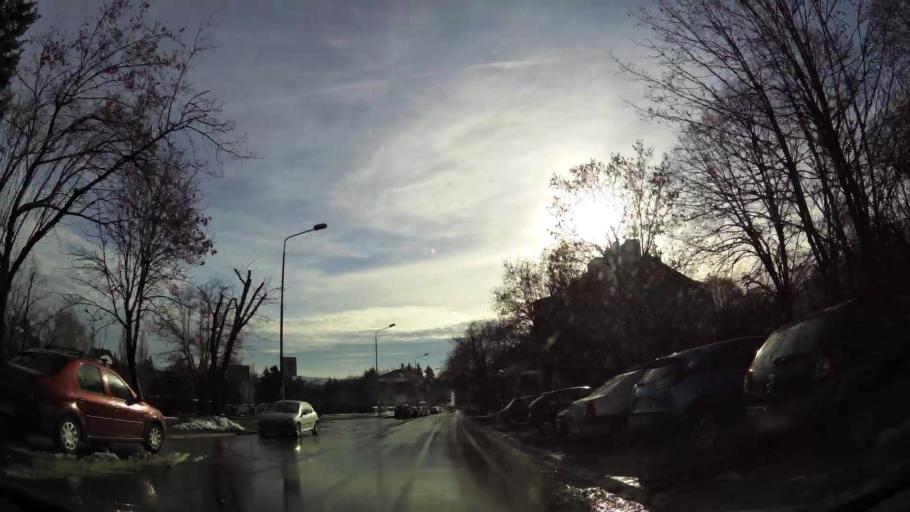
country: RS
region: Central Serbia
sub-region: Belgrade
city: Rakovica
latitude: 44.7266
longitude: 20.4213
